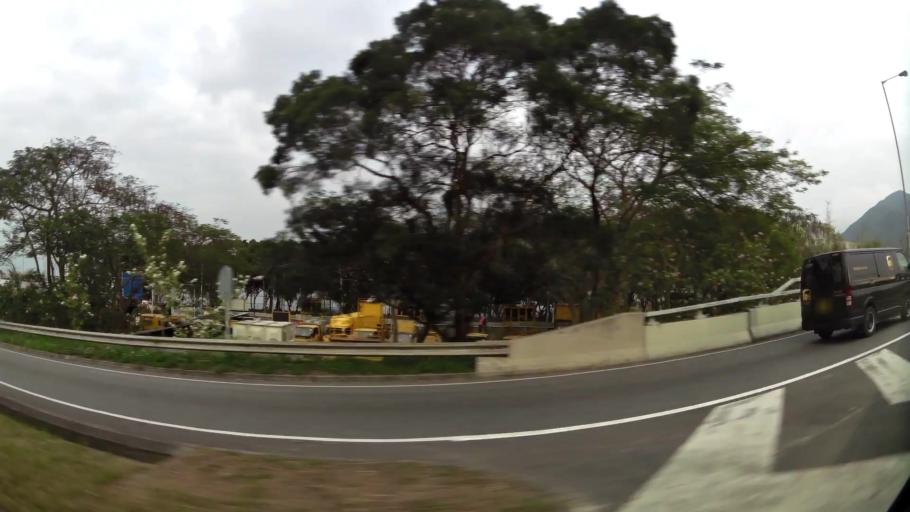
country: HK
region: Sha Tin
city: Sha Tin
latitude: 22.4109
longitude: 114.2128
